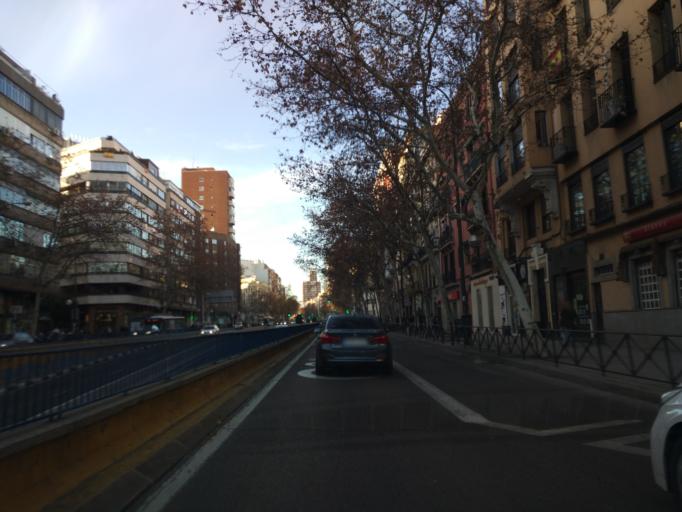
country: ES
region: Madrid
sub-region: Provincia de Madrid
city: Salamanca
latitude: 40.4306
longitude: -3.6708
